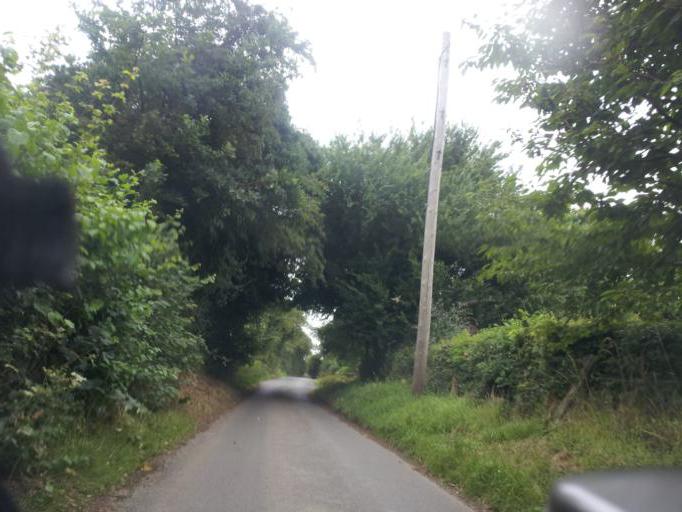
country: GB
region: England
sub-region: Kent
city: Newington
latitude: 51.3602
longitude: 0.6657
